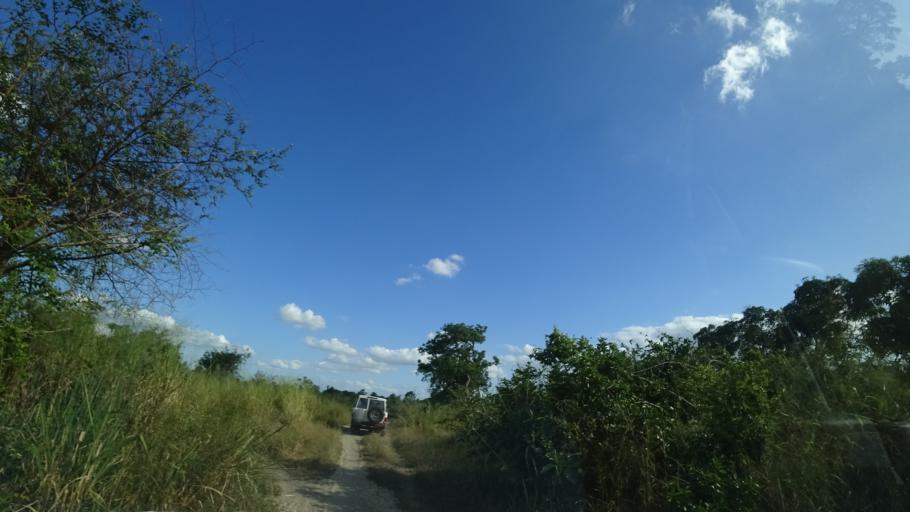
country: MZ
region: Sofala
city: Dondo
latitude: -19.3418
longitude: 34.5827
